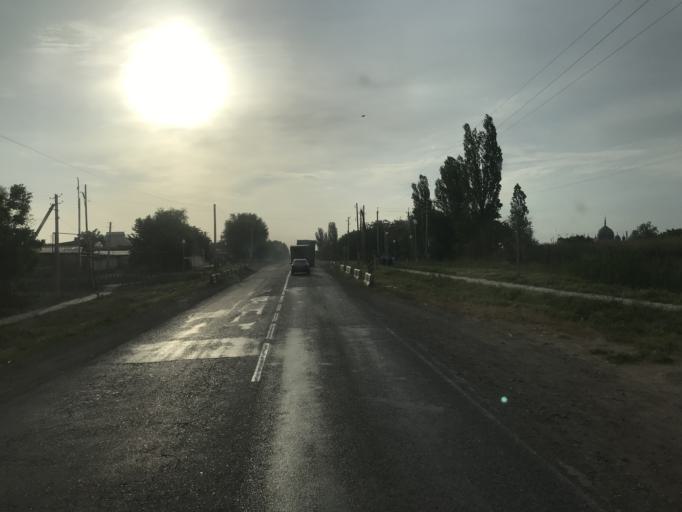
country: UZ
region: Toshkent
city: Salor
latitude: 41.4937
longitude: 69.3125
